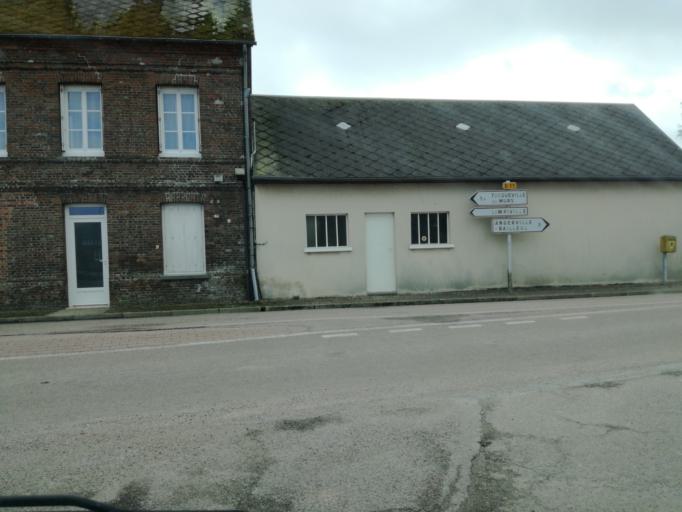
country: FR
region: Haute-Normandie
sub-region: Departement de la Seine-Maritime
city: Yebleron
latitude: 49.6733
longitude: 0.4927
